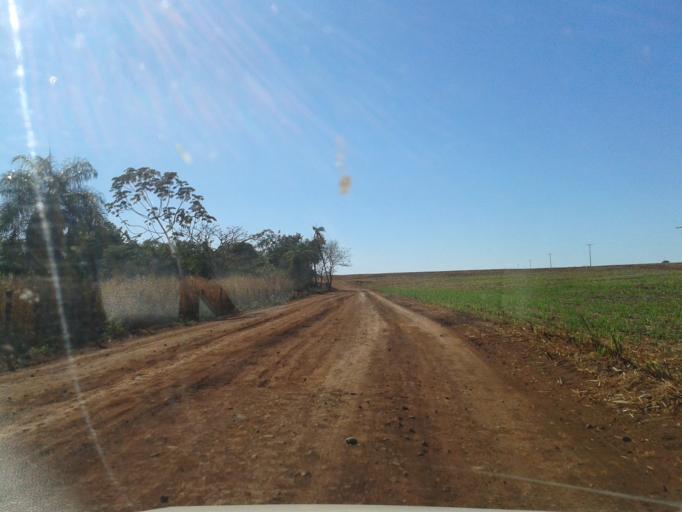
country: BR
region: Minas Gerais
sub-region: Centralina
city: Centralina
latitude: -18.5913
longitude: -49.1676
